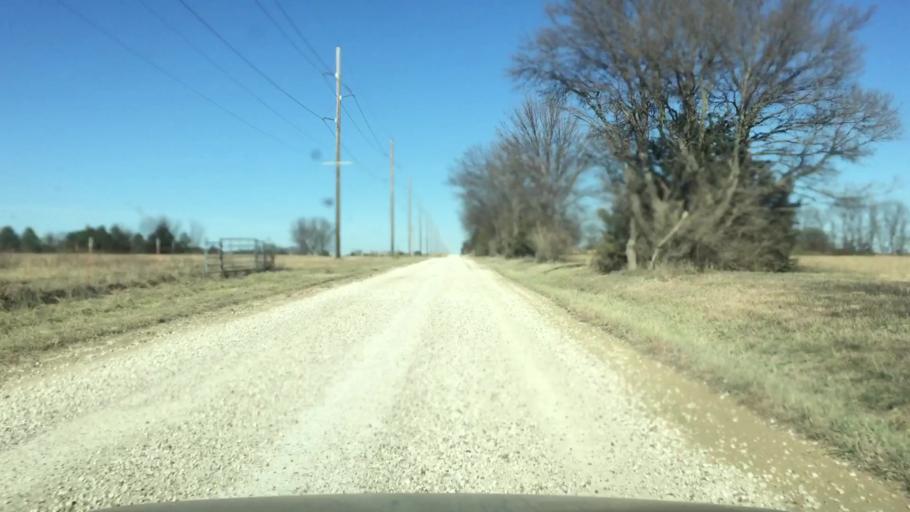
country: US
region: Kansas
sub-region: Allen County
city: Humboldt
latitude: 37.8288
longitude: -95.4185
